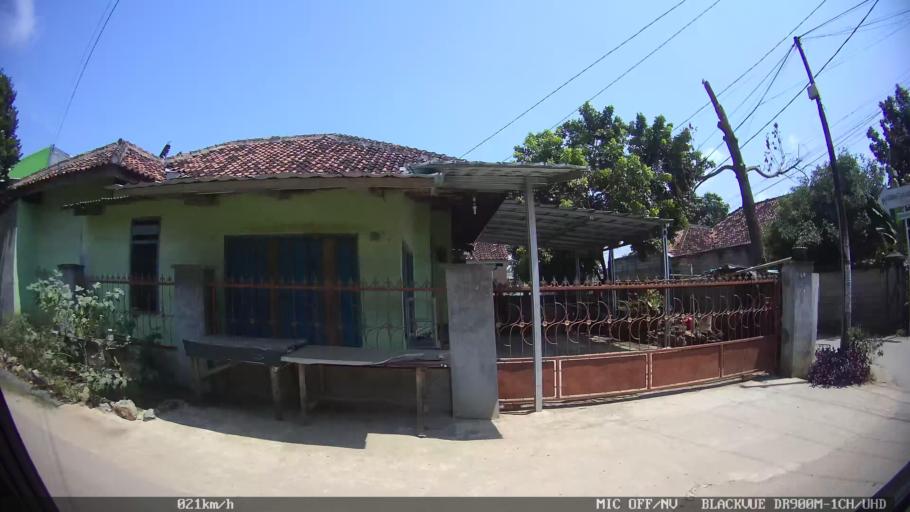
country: ID
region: Lampung
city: Kedaton
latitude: -5.3593
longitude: 105.2747
